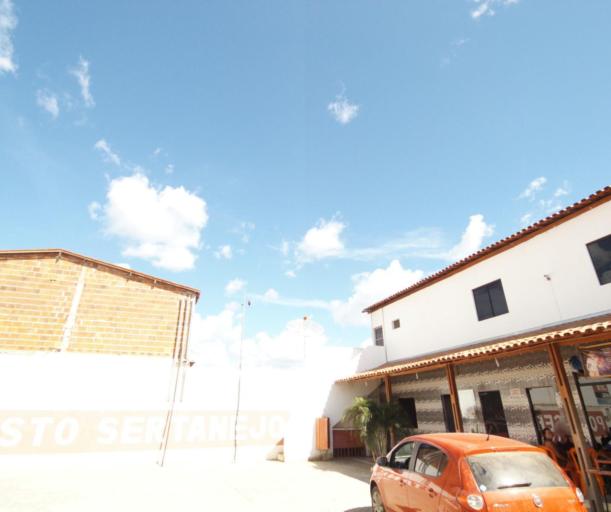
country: BR
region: Bahia
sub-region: Pocoes
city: Pocoes
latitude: -14.2426
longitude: -40.7647
